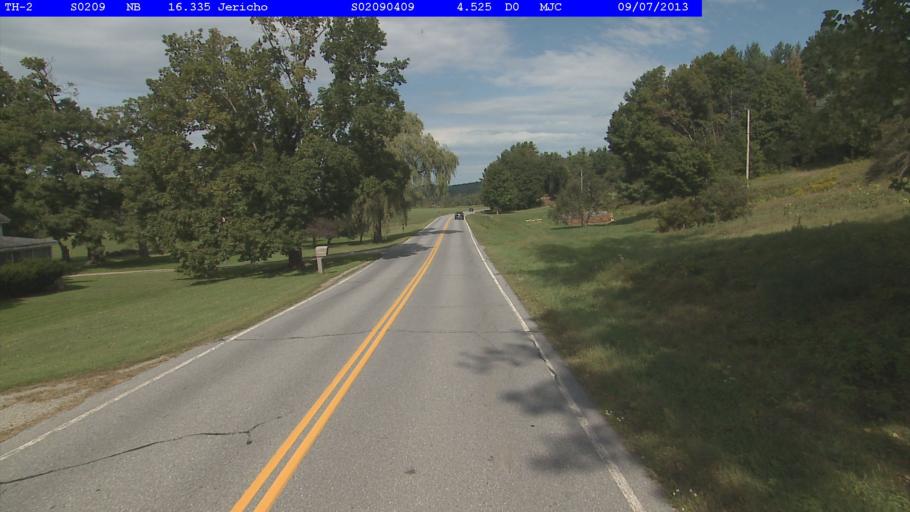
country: US
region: Vermont
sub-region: Chittenden County
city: Jericho
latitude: 44.4884
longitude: -72.9796
